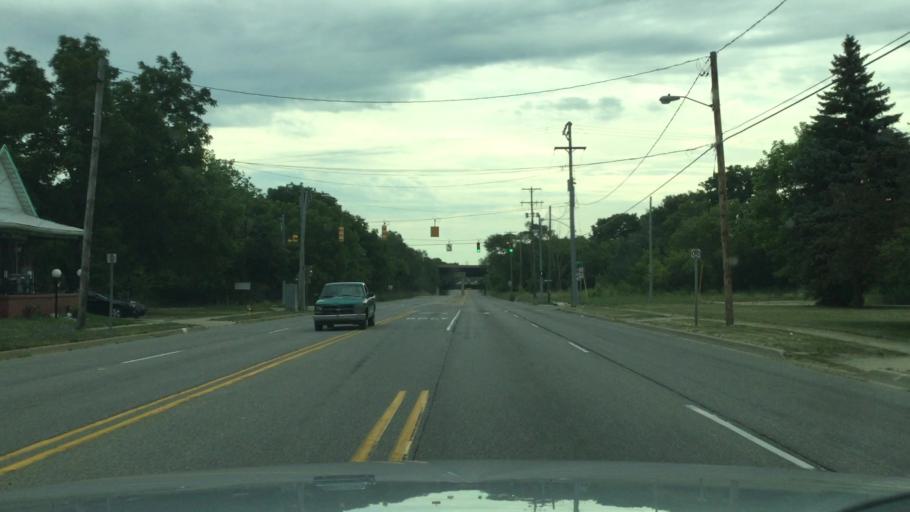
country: US
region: Michigan
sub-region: Genesee County
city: Beecher
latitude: 43.0613
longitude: -83.6835
